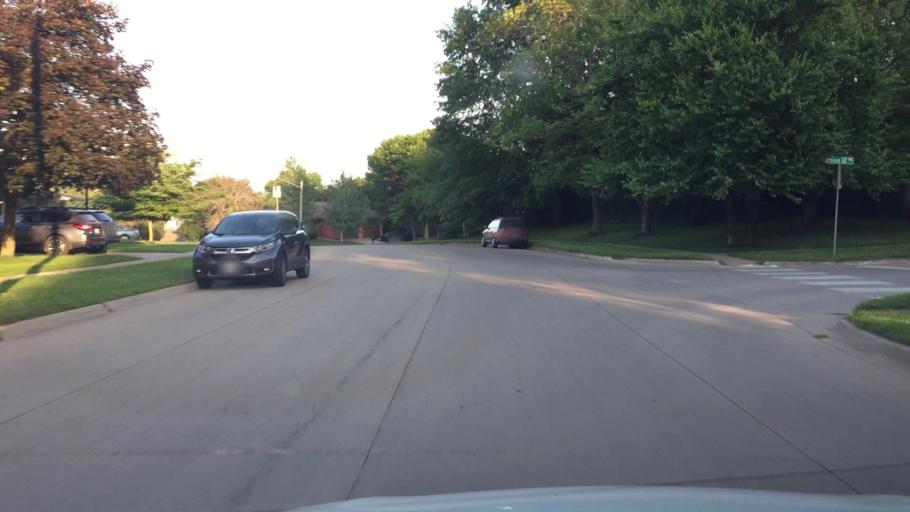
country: US
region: Iowa
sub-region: Johnson County
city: Iowa City
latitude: 41.6605
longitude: -91.4857
